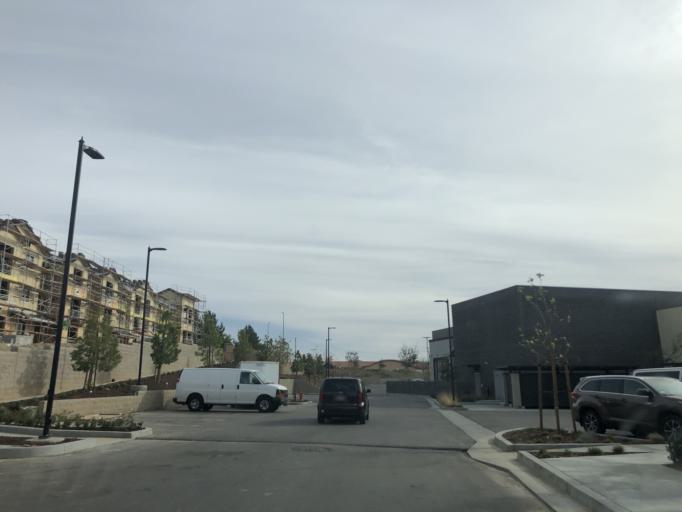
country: US
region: California
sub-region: Los Angeles County
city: Chatsworth
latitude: 34.2775
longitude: -118.5723
